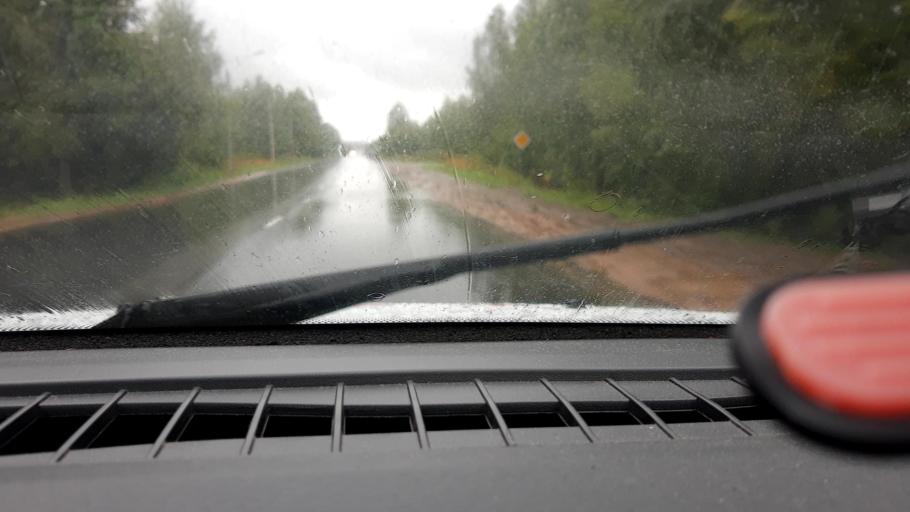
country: RU
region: Nizjnij Novgorod
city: Lyskovo
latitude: 56.0173
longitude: 45.0148
